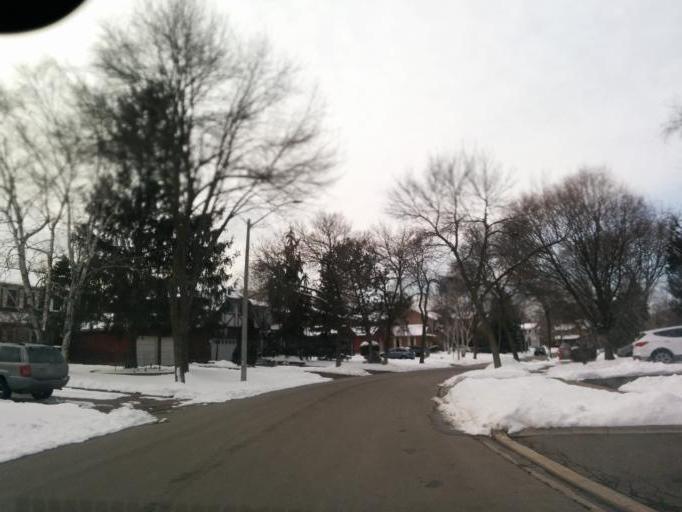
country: CA
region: Ontario
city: Mississauga
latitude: 43.5377
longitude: -79.6598
